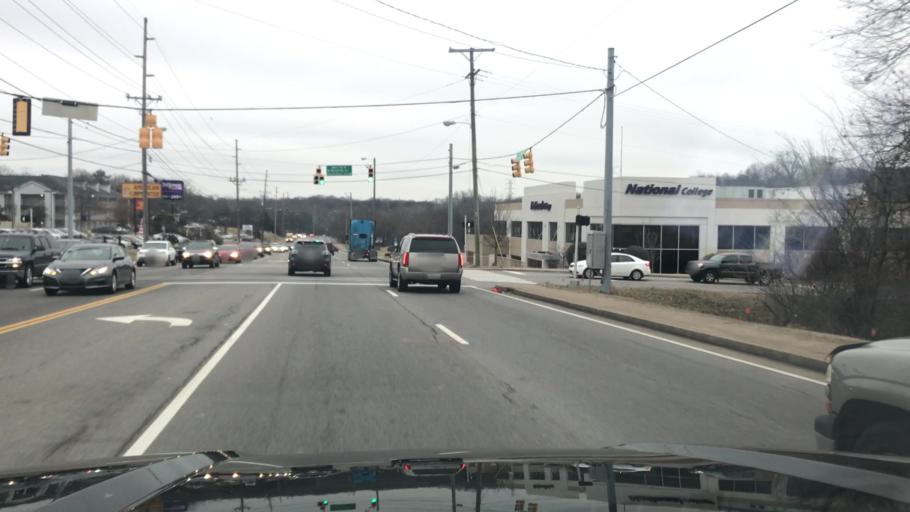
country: US
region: Tennessee
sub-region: Williamson County
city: Brentwood Estates
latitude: 36.0453
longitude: -86.7022
